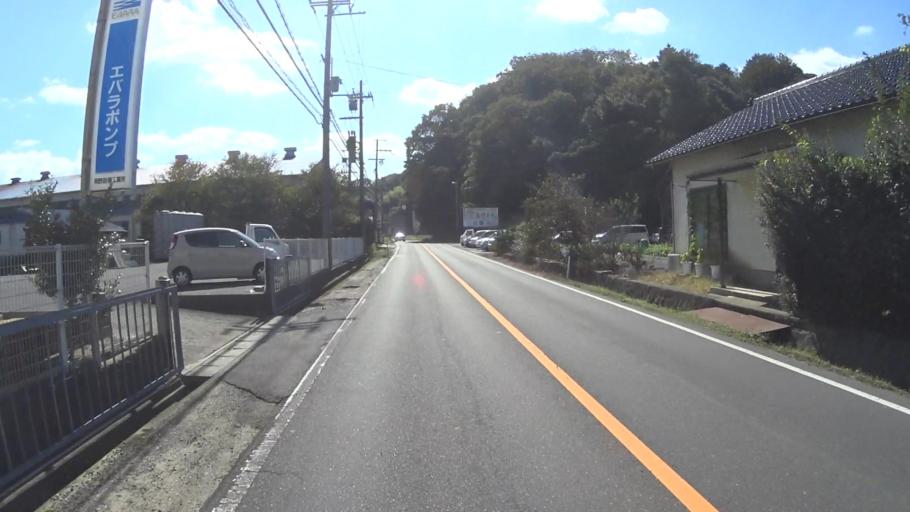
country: JP
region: Kyoto
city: Miyazu
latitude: 35.6670
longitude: 135.0279
